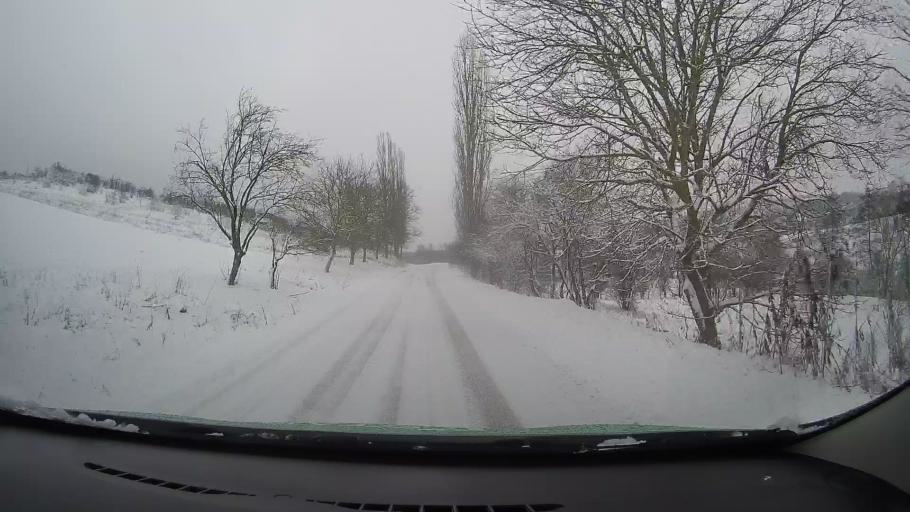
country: RO
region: Hunedoara
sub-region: Comuna Carjiti
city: Carjiti
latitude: 45.8255
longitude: 22.8539
